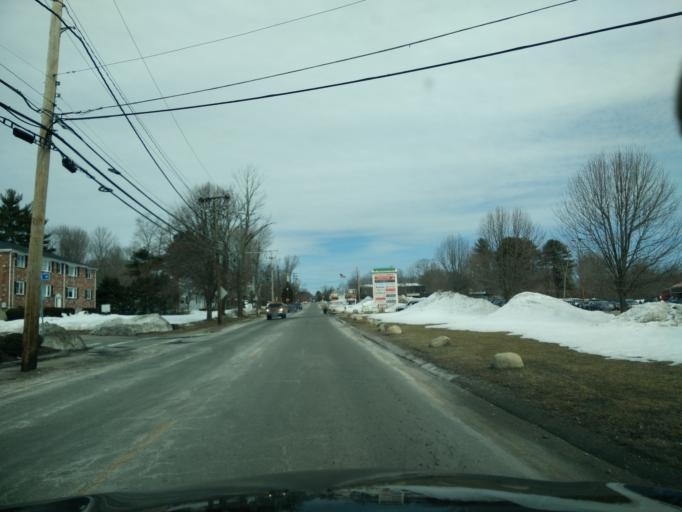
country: US
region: Massachusetts
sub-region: Norfolk County
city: Walpole
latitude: 42.1541
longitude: -71.2465
